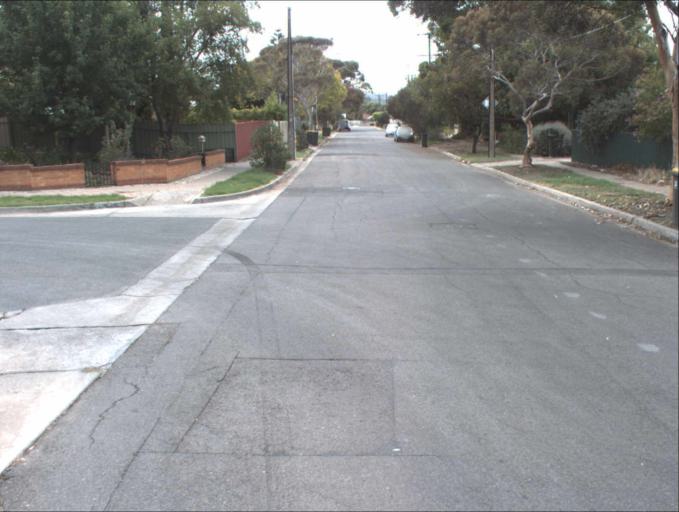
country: AU
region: South Australia
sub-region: Campbelltown
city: Paradise
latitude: -34.8584
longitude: 138.6645
